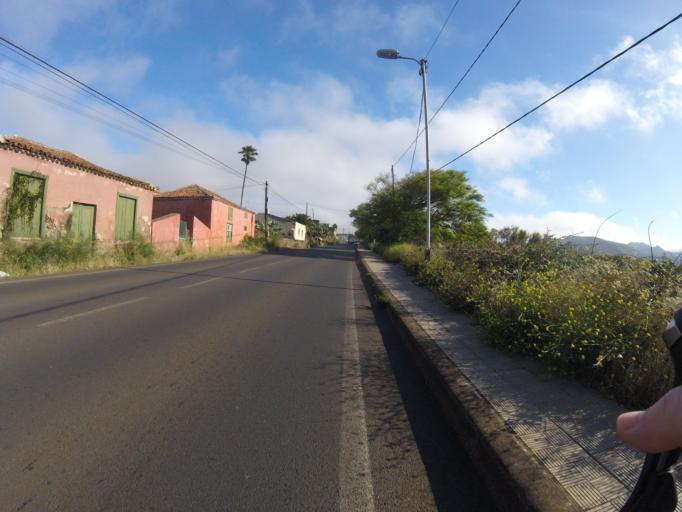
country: ES
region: Canary Islands
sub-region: Provincia de Santa Cruz de Tenerife
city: La Laguna
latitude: 28.4748
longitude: -16.3180
